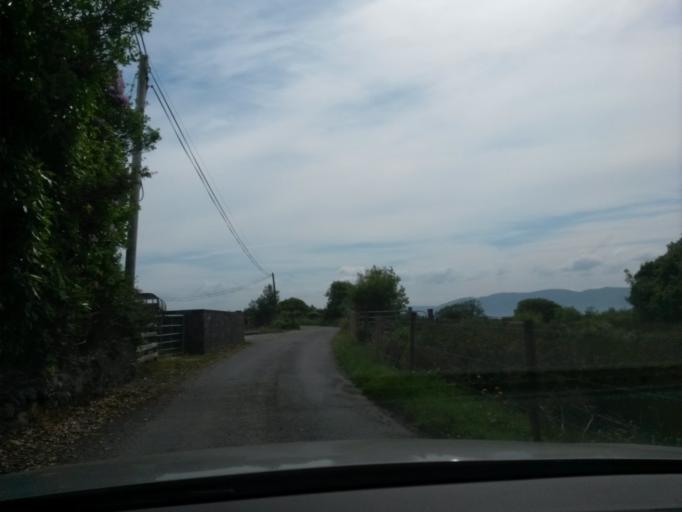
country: IE
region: Munster
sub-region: Ciarrai
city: Cahersiveen
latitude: 51.8076
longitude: -9.9824
